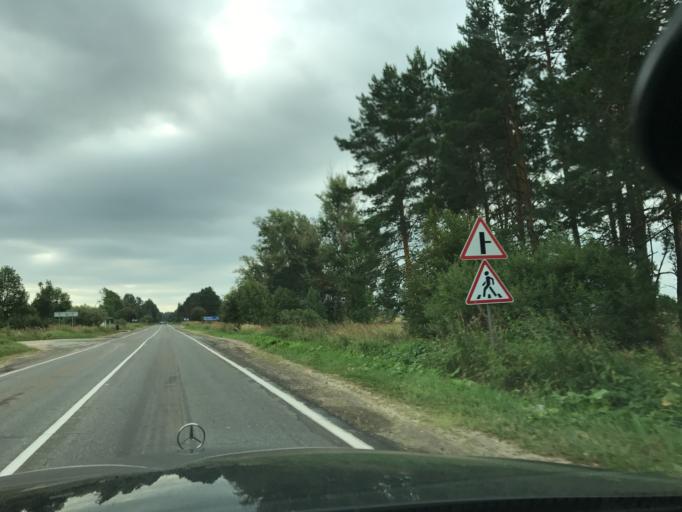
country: RU
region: Vladimir
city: Galitsy
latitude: 56.1864
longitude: 42.7709
